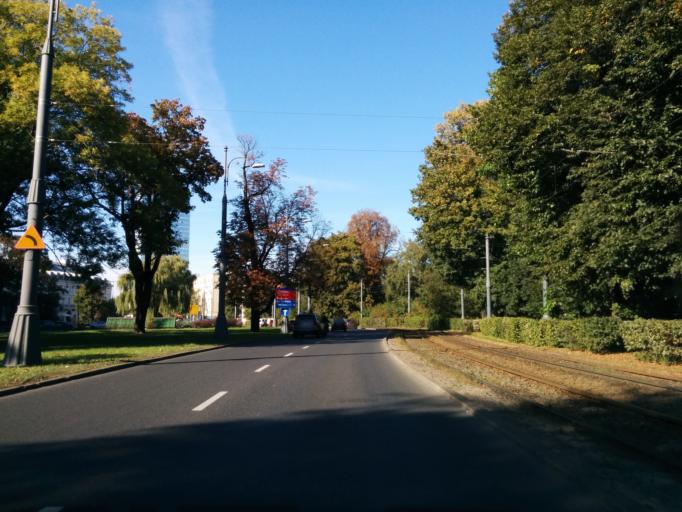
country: PL
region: Masovian Voivodeship
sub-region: Warszawa
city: Warsaw
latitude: 52.2403
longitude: 21.0048
